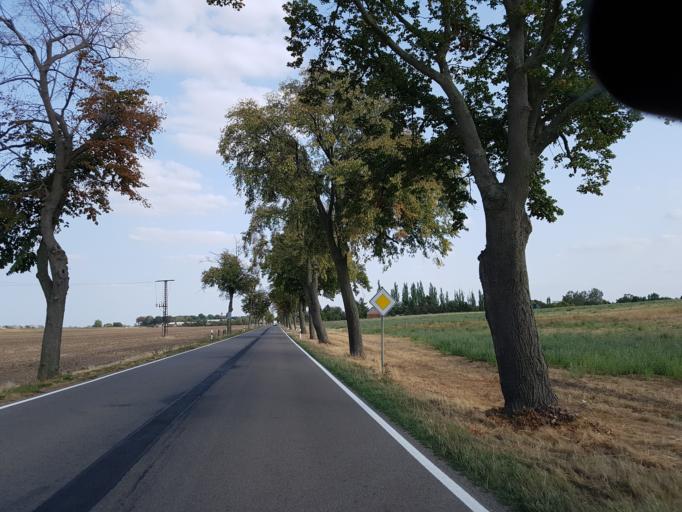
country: DE
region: Saxony-Anhalt
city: Pretzsch
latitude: 51.7228
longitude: 12.7883
